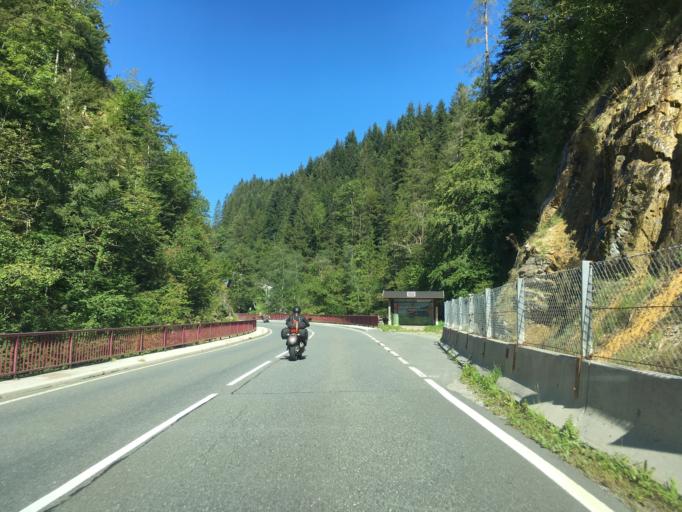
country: AT
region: Salzburg
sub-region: Politischer Bezirk Hallein
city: Abtenau
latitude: 47.5443
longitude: 13.4193
